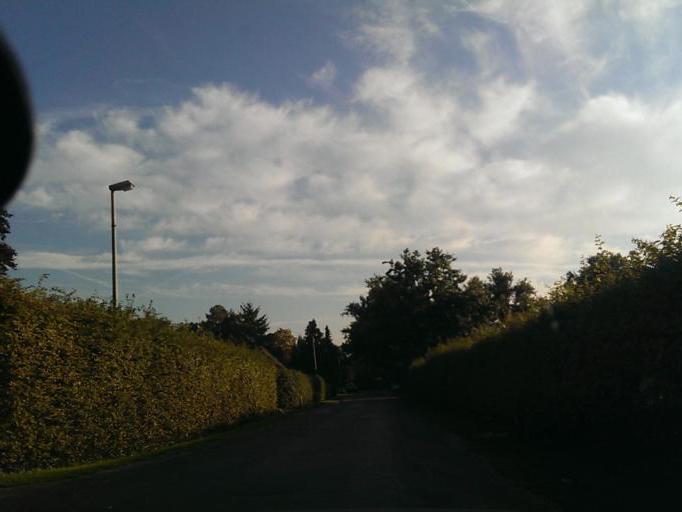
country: DE
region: Lower Saxony
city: Elze
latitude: 52.5872
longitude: 9.7382
